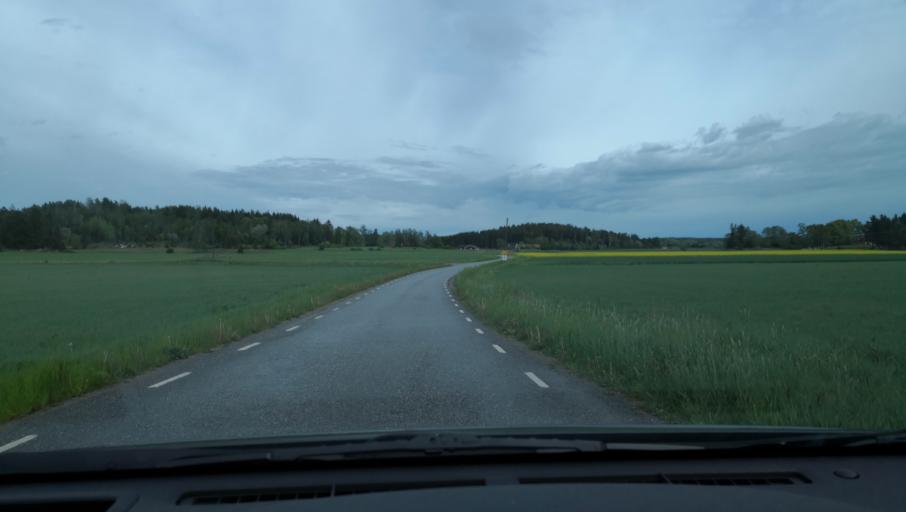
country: SE
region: Uppsala
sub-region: Enkopings Kommun
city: Orsundsbro
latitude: 59.7071
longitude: 17.3774
